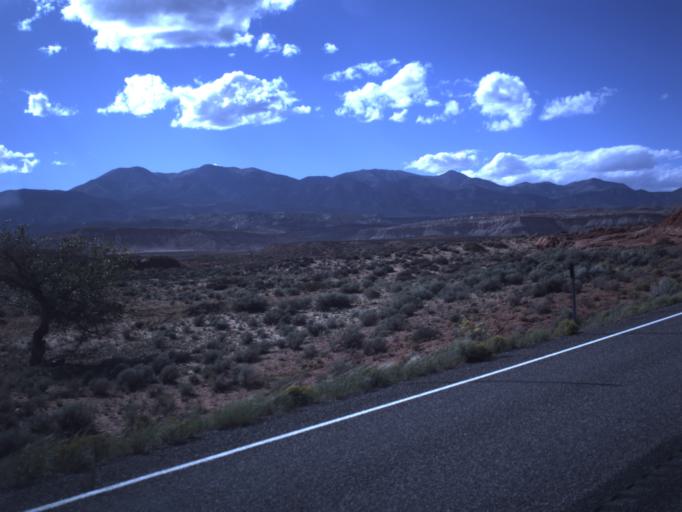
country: US
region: Utah
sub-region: Wayne County
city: Loa
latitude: 38.0619
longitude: -110.5980
